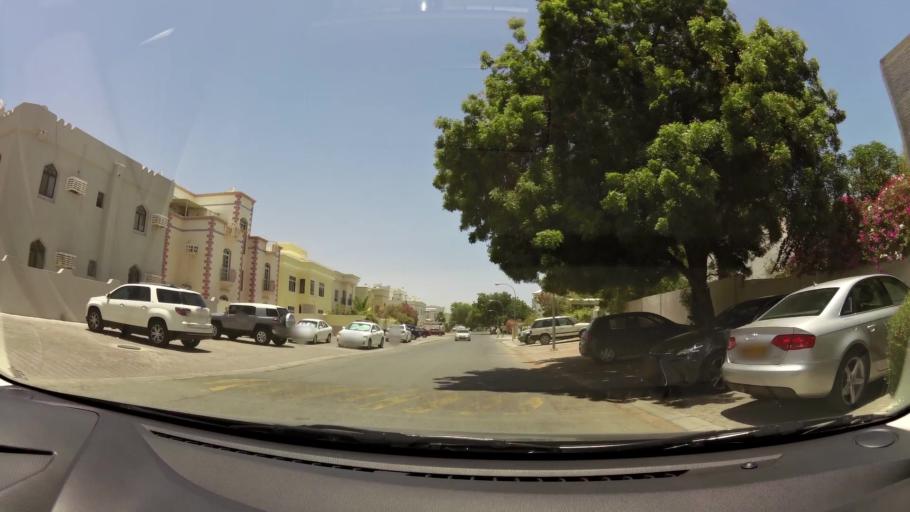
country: OM
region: Muhafazat Masqat
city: Bawshar
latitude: 23.5976
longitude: 58.3940
